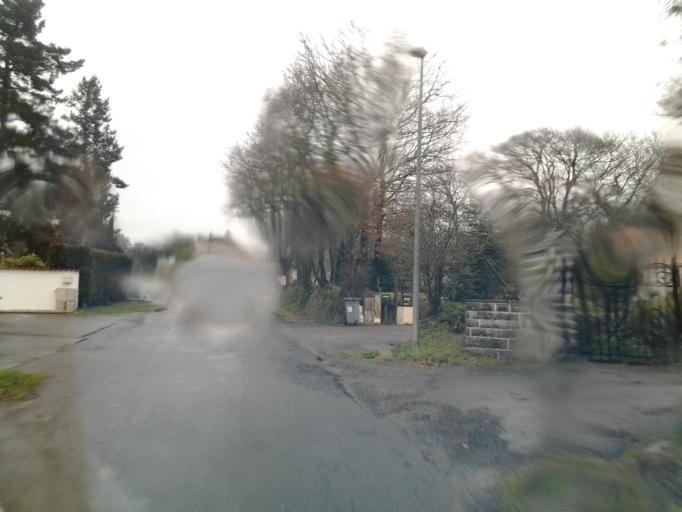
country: FR
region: Pays de la Loire
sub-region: Departement de la Vendee
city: Les Clouzeaux
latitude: 46.6452
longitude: -1.5364
